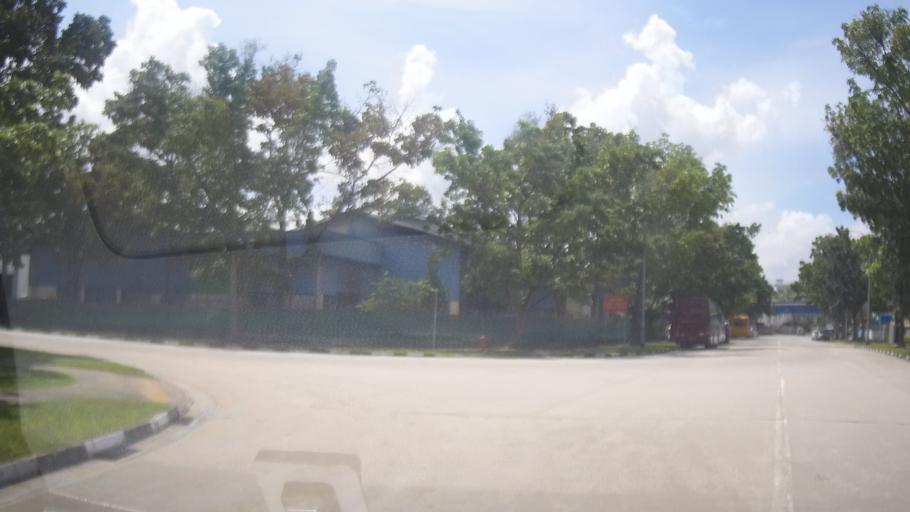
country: MY
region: Johor
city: Johor Bahru
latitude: 1.4069
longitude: 103.7479
